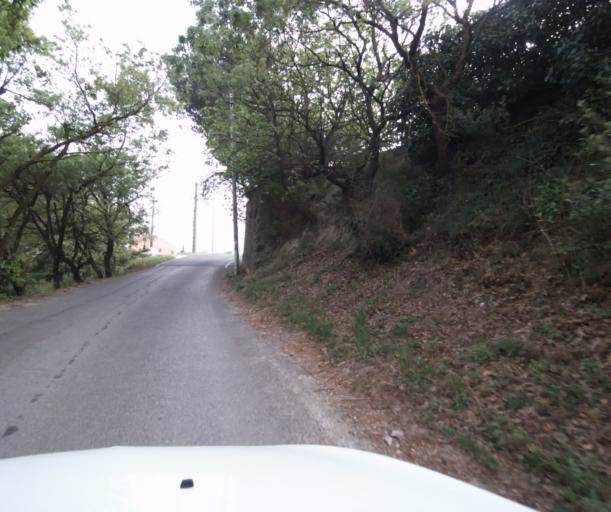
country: FR
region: Provence-Alpes-Cote d'Azur
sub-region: Departement du Var
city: Carqueiranne
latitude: 43.1077
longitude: 6.1044
